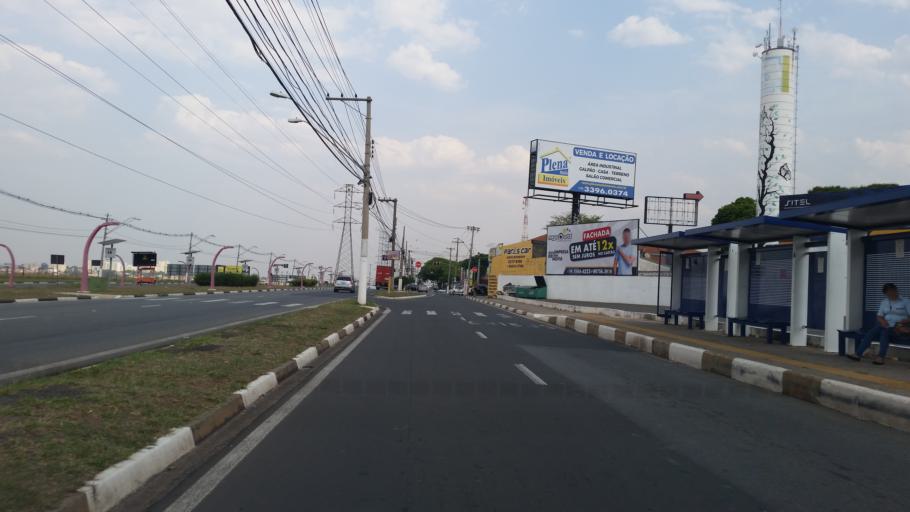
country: BR
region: Sao Paulo
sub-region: Hortolandia
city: Hortolandia
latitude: -22.8876
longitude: -47.1933
